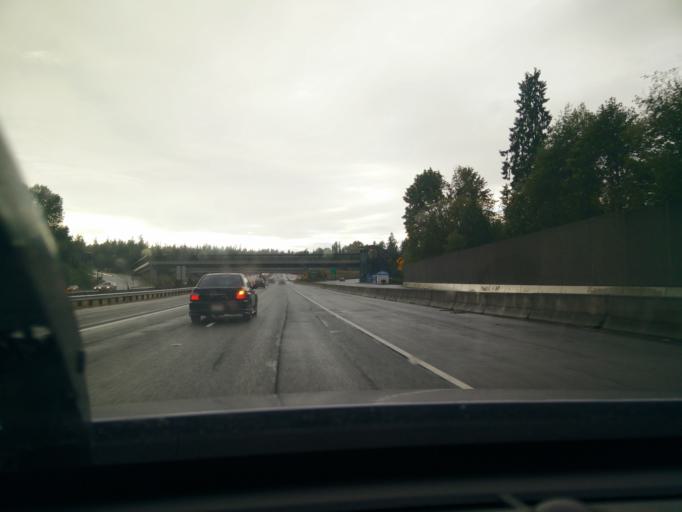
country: US
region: Washington
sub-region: King County
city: Bothell
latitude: 47.7928
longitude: -122.2096
